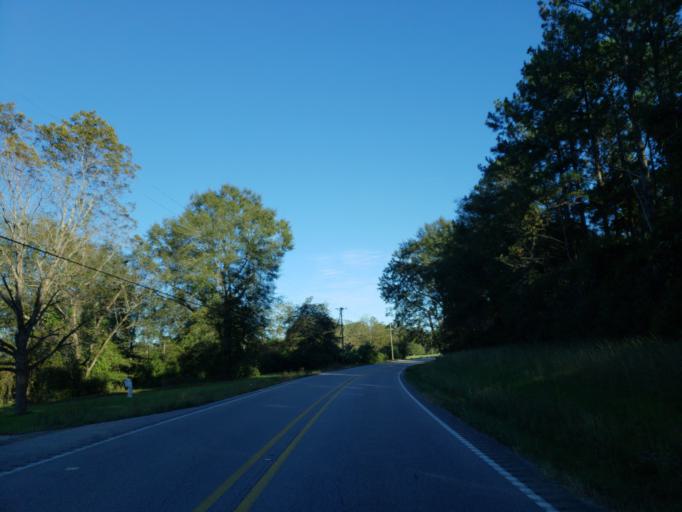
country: US
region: Mississippi
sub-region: Perry County
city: Richton
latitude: 31.3580
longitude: -88.9611
